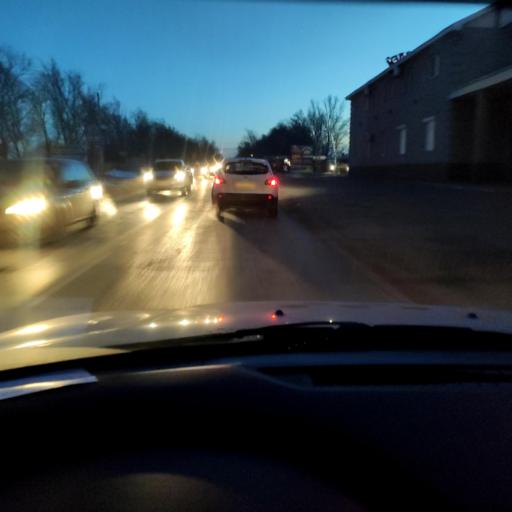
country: RU
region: Samara
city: Tol'yatti
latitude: 53.5553
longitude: 49.3939
